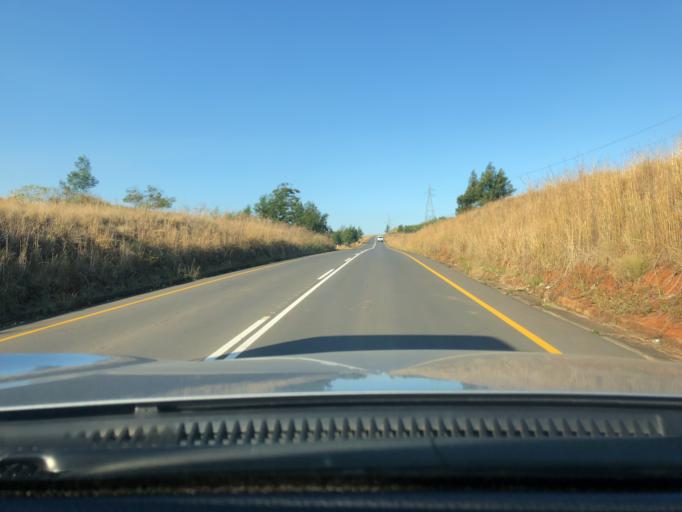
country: ZA
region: KwaZulu-Natal
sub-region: Sisonke District Municipality
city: Ixopo
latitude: -30.3401
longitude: 30.1666
